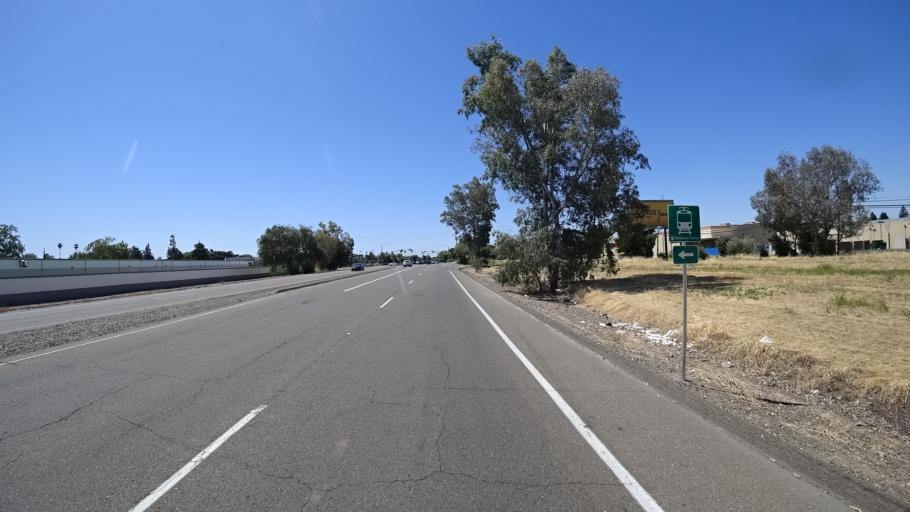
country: US
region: California
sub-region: Sacramento County
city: Parkway
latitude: 38.4975
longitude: -121.5062
